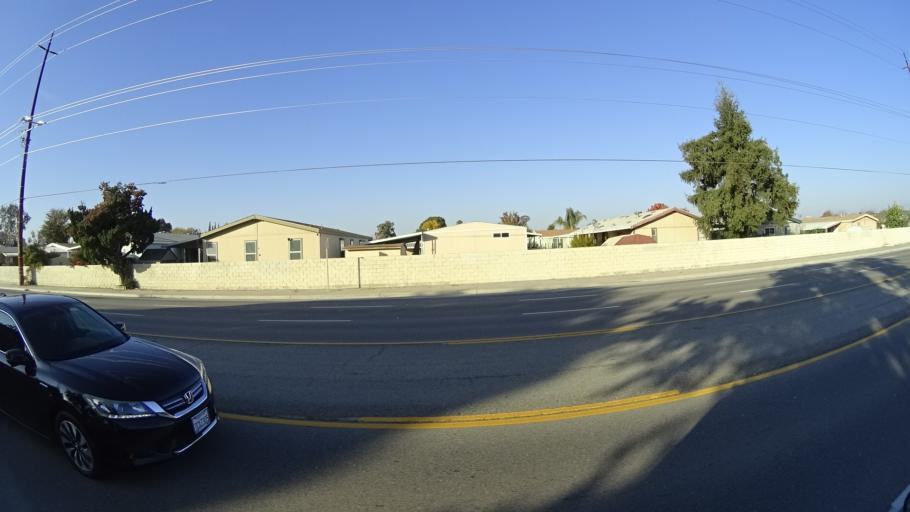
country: US
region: California
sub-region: Kern County
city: Greenfield
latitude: 35.2959
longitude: -119.0514
